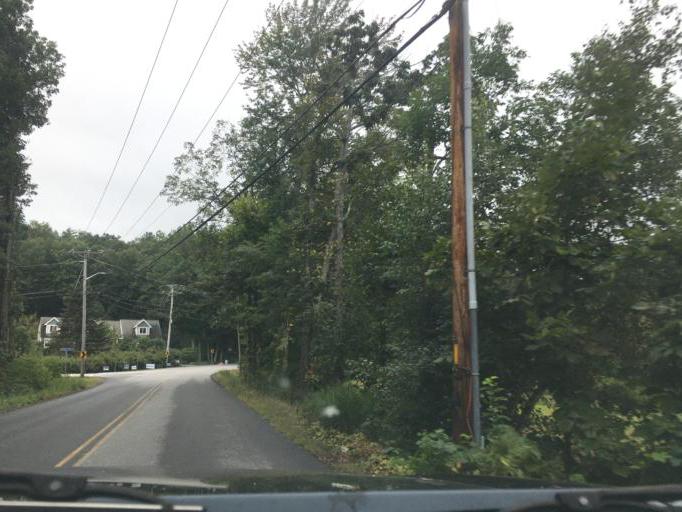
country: US
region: New Hampshire
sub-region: Rockingham County
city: Exeter
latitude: 42.9893
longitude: -70.8913
